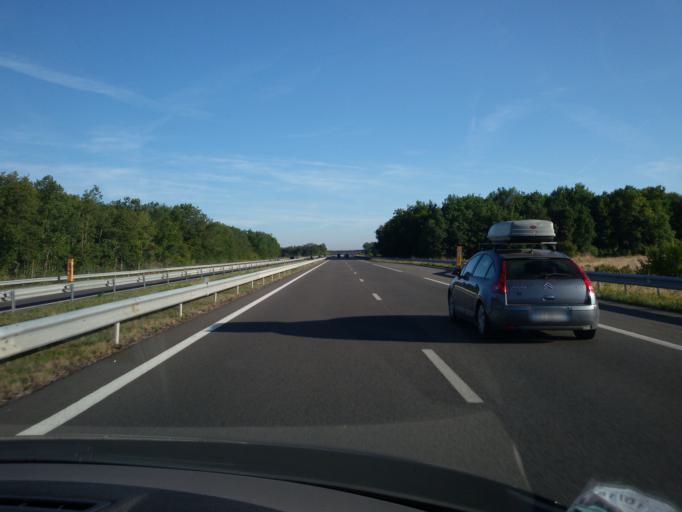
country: FR
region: Centre
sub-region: Departement du Cher
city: Levet
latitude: 46.8874
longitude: 2.4191
